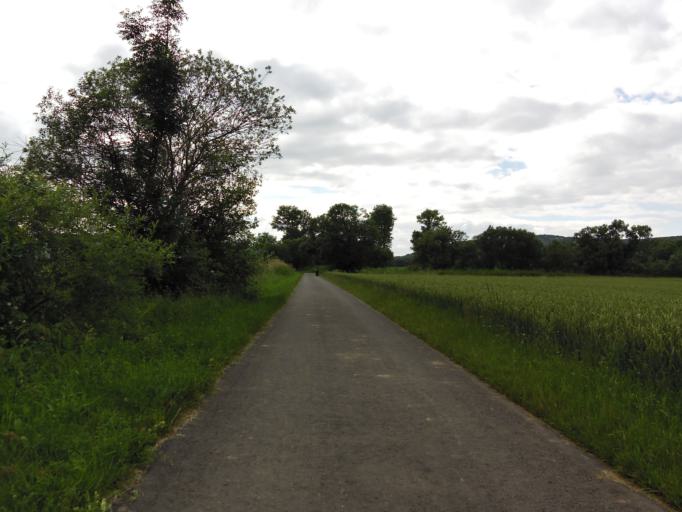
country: DE
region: Thuringia
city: Creuzburg
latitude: 51.0455
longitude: 10.2444
